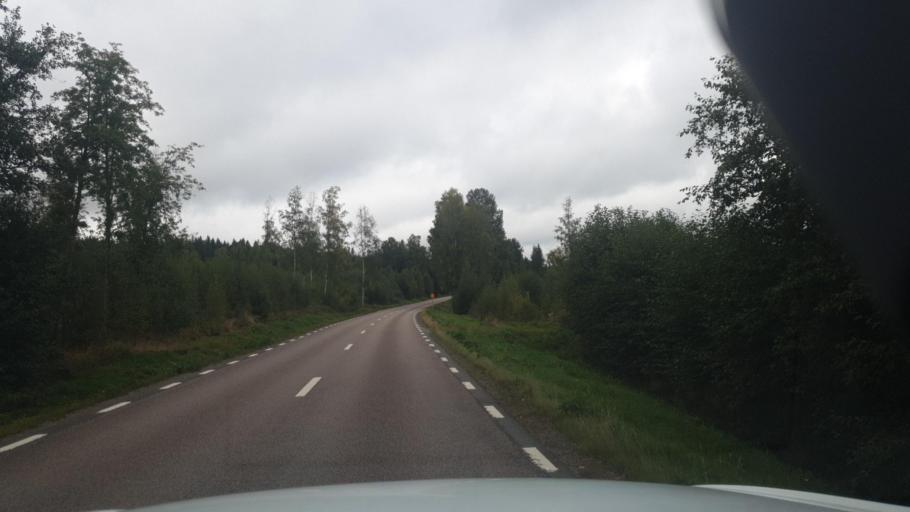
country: SE
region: Vaermland
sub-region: Sunne Kommun
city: Sunne
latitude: 59.8316
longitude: 12.9718
